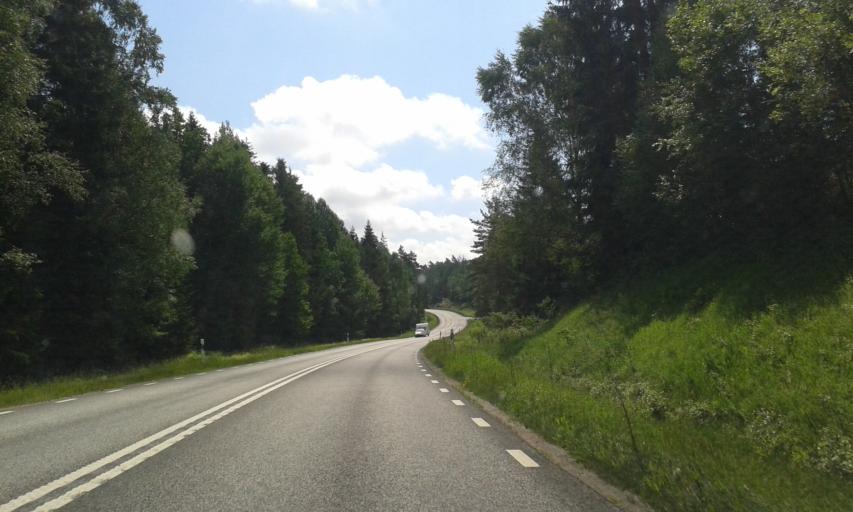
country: SE
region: Joenkoeping
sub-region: Varnamo Kommun
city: Bredaryd
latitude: 57.2267
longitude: 13.6848
